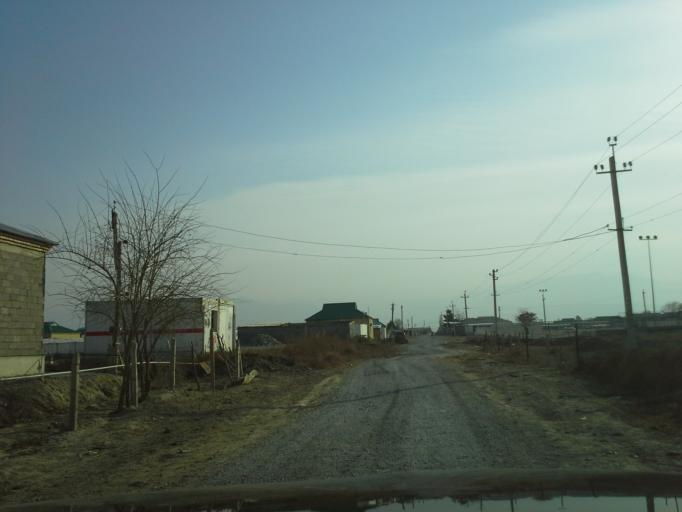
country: TM
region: Ahal
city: Abadan
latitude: 38.1778
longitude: 58.0459
